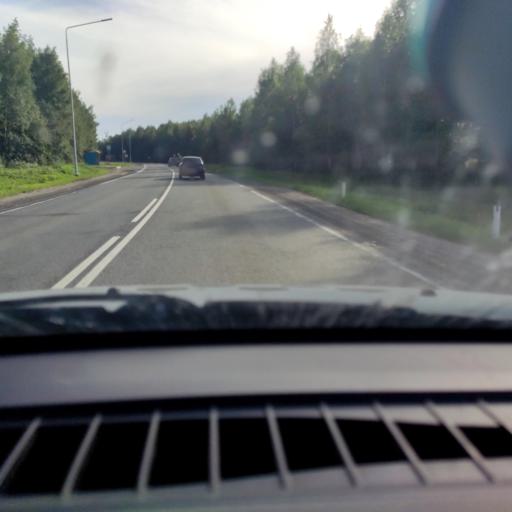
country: RU
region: Kirov
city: Vakhrushi
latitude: 58.6664
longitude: 49.9312
